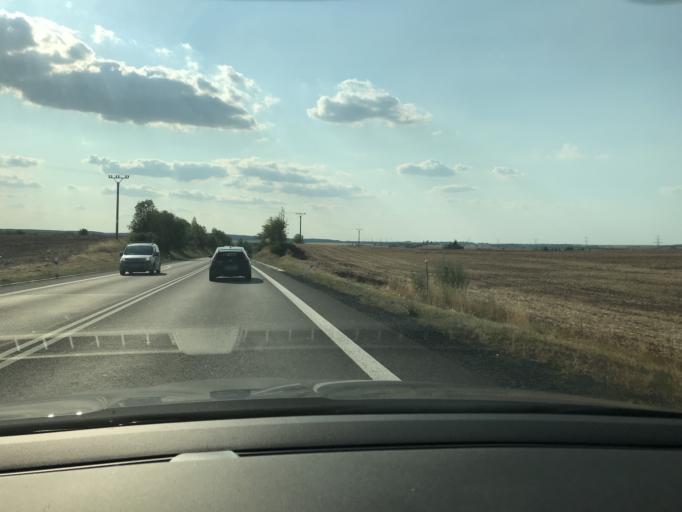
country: CZ
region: Central Bohemia
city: Klobuky
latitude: 50.2730
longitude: 13.9869
